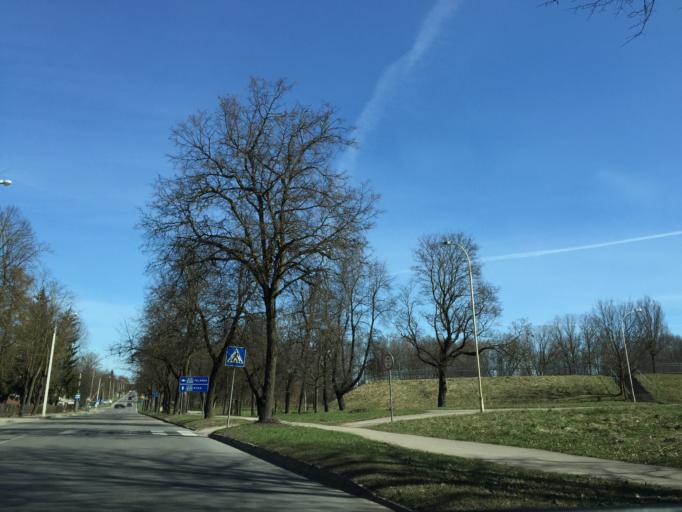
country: LT
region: Siauliu apskritis
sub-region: Siauliai
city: Siauliai
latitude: 55.9400
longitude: 23.3112
